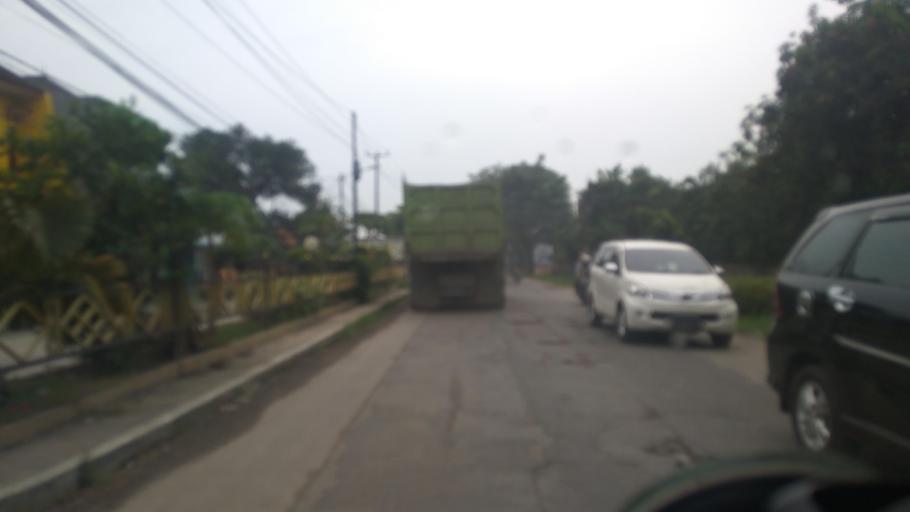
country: ID
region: West Java
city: Bekasi
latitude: -6.1947
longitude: 107.0380
